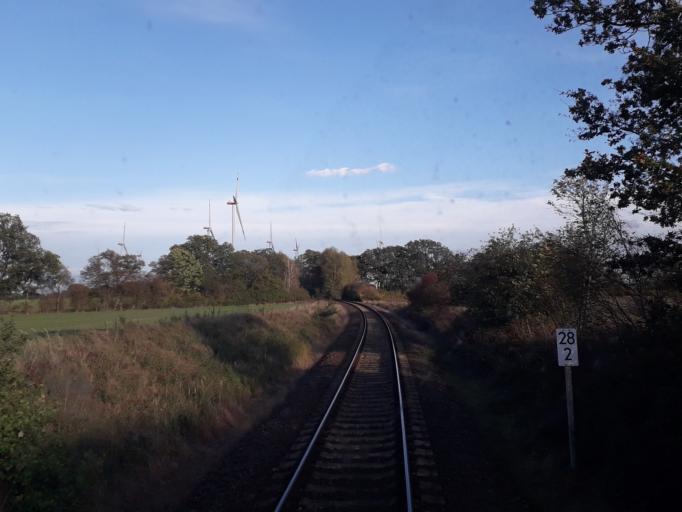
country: DE
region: Brandenburg
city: Gross Pankow
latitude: 53.1291
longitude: 12.0824
